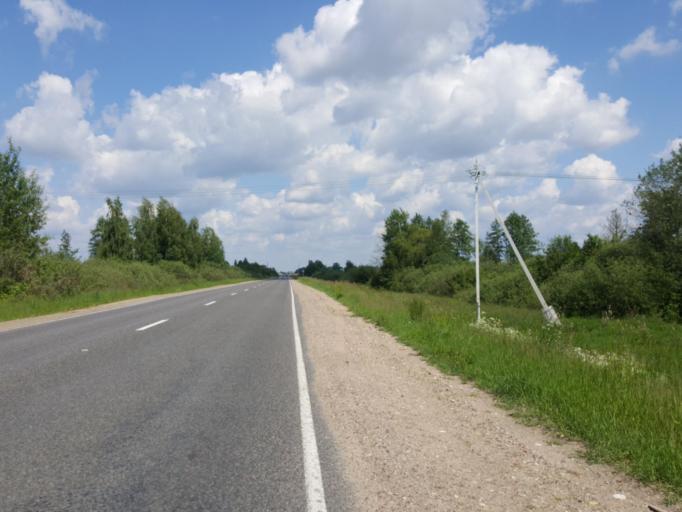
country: BY
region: Brest
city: Kamyanyets
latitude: 52.3888
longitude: 23.7869
